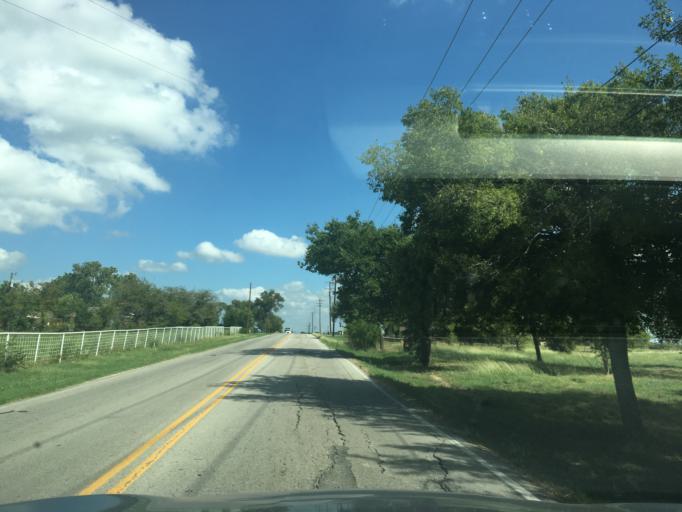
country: US
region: Texas
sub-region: Dallas County
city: Sachse
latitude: 32.9542
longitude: -96.5655
